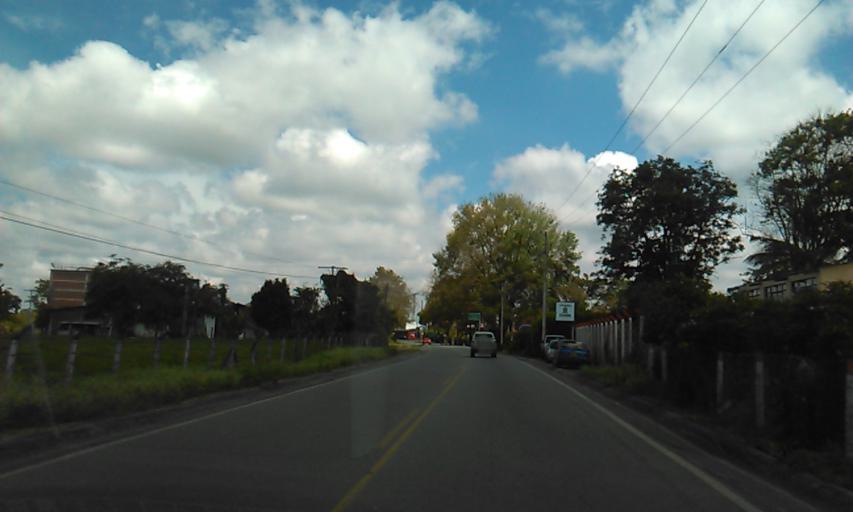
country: CO
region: Quindio
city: Armenia
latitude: 4.4792
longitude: -75.6996
